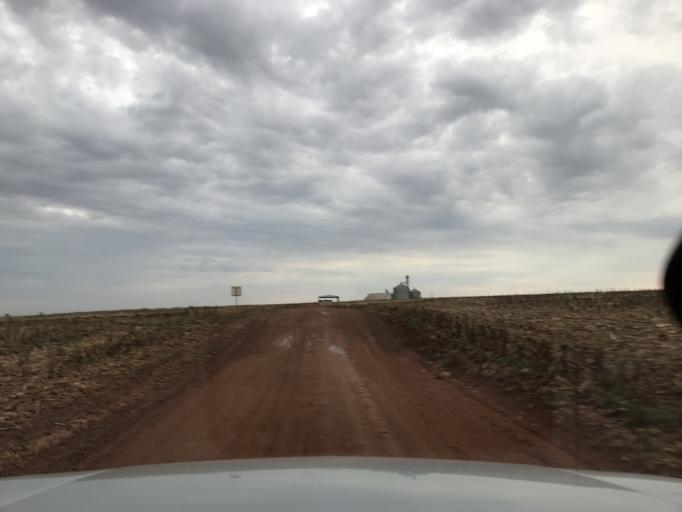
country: BR
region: Parana
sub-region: Palotina
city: Palotina
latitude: -24.2246
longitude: -53.8388
